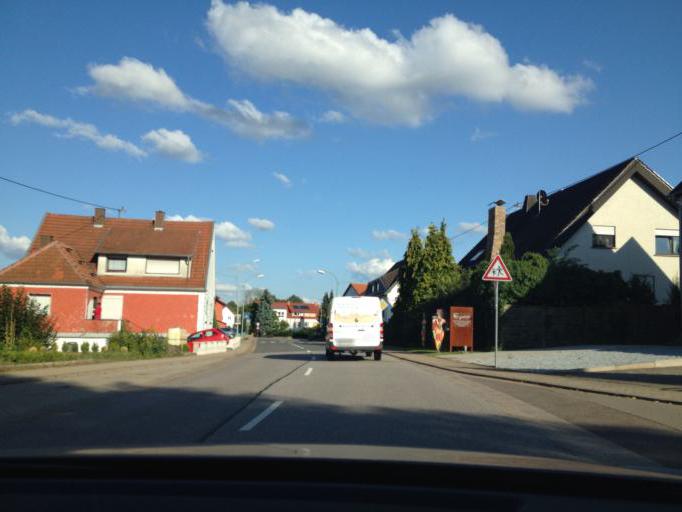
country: DE
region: Saarland
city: Eppelborn
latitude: 49.4751
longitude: 6.9590
